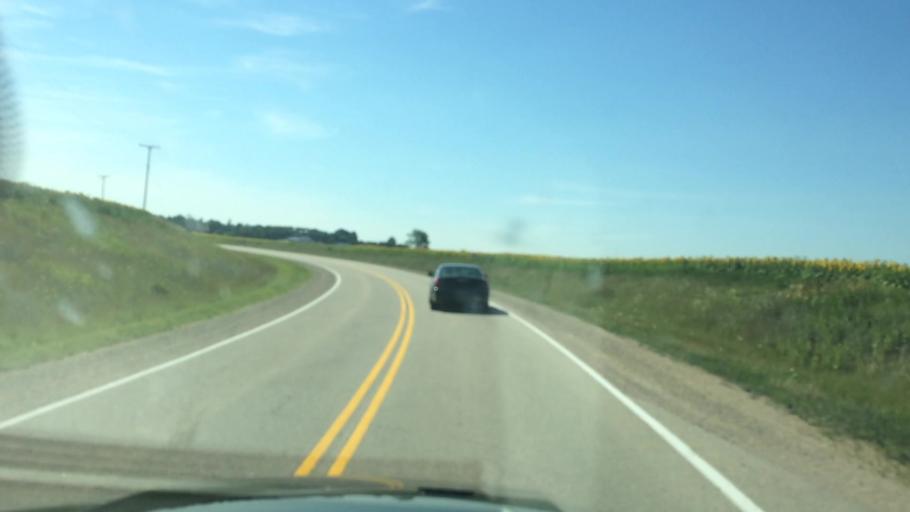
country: US
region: Wisconsin
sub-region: Shawano County
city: Bonduel
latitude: 44.7887
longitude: -88.3522
